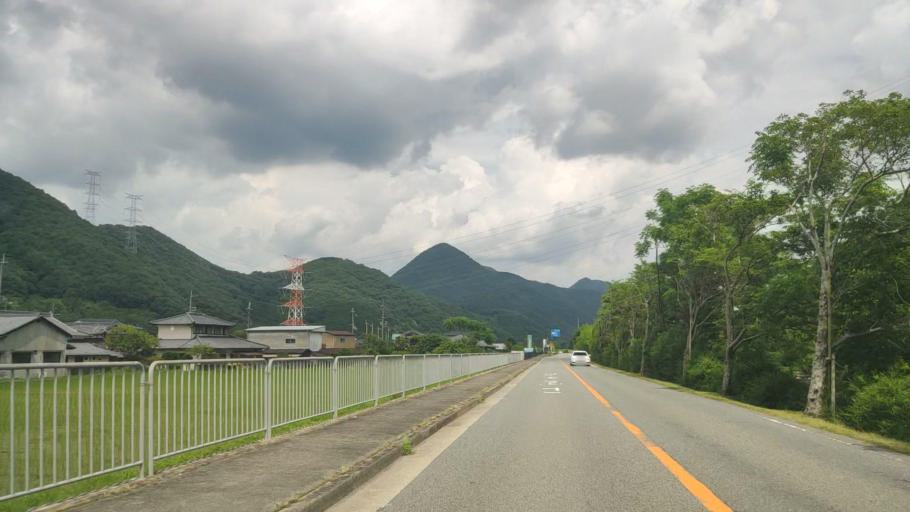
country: JP
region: Hyogo
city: Yamazakicho-nakabirose
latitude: 34.9411
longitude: 134.4929
